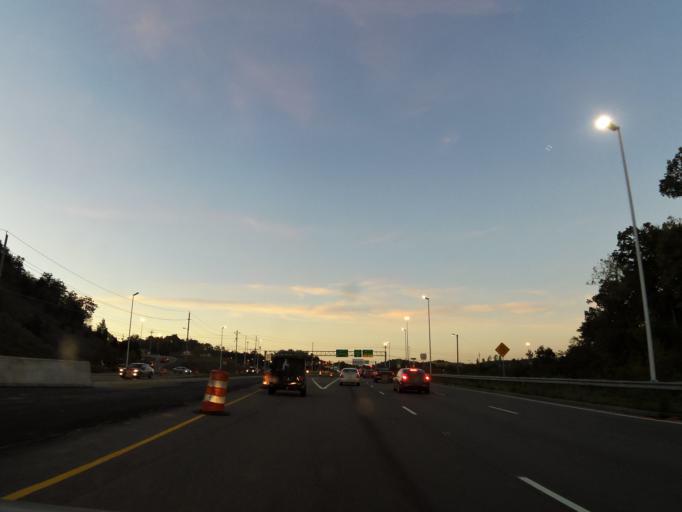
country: US
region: Tennessee
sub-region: Sevier County
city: Sevierville
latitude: 35.9794
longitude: -83.6076
